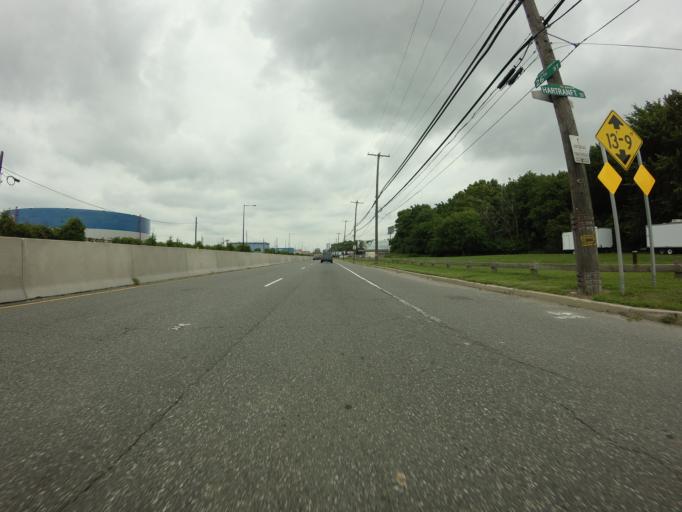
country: US
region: New Jersey
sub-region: Gloucester County
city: National Park
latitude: 39.9123
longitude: -75.1925
